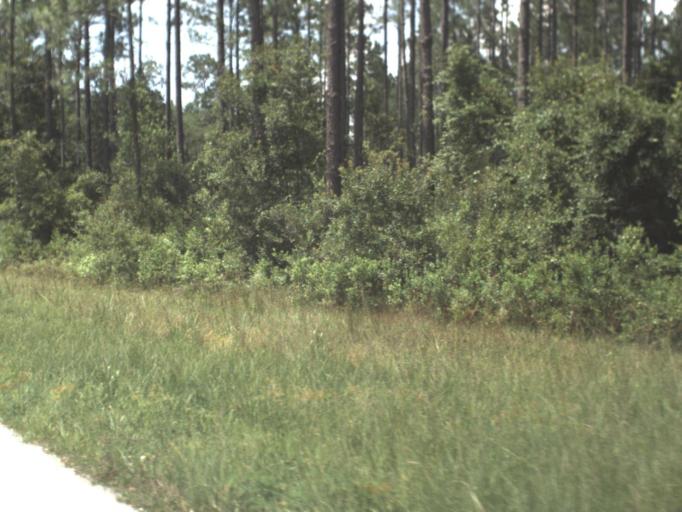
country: US
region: Florida
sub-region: Columbia County
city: Five Points
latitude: 30.5784
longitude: -82.4620
